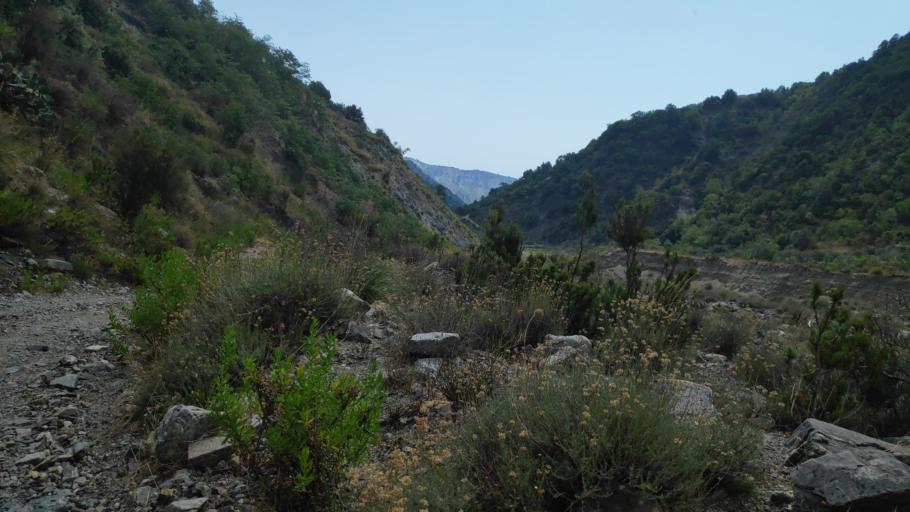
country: IT
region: Calabria
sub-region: Provincia di Reggio Calabria
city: Bivongi
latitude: 38.4943
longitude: 16.4480
